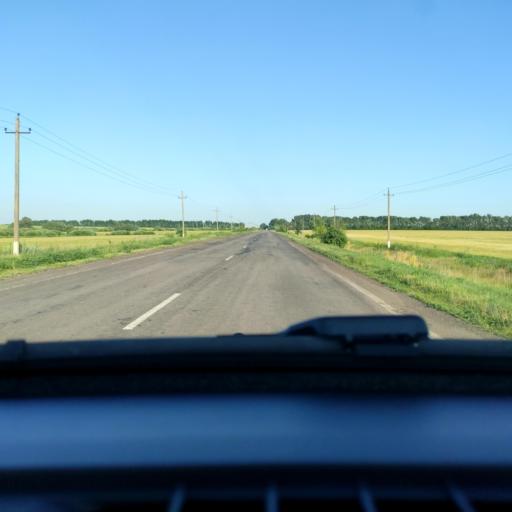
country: RU
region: Voronezj
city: Kashirskoye
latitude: 51.4948
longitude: 39.8396
